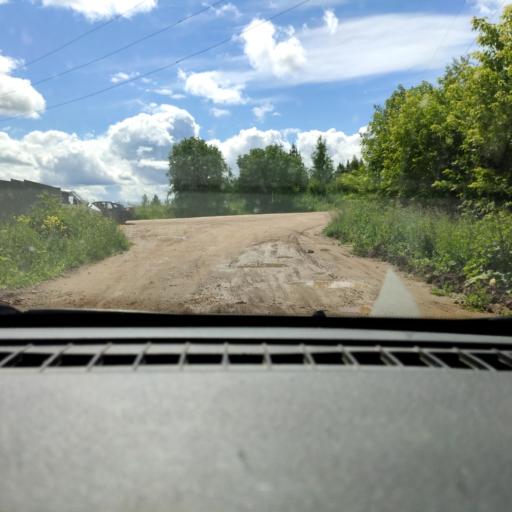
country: RU
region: Perm
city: Overyata
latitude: 58.1338
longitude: 55.8255
